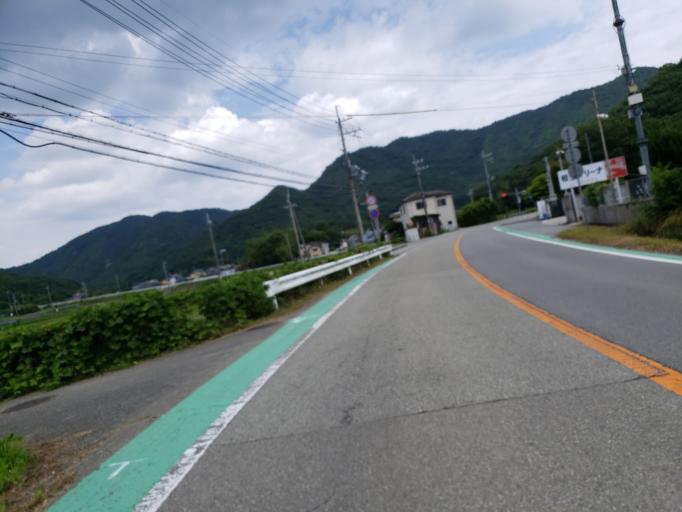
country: JP
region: Hyogo
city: Aioi
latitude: 34.7873
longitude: 134.4785
